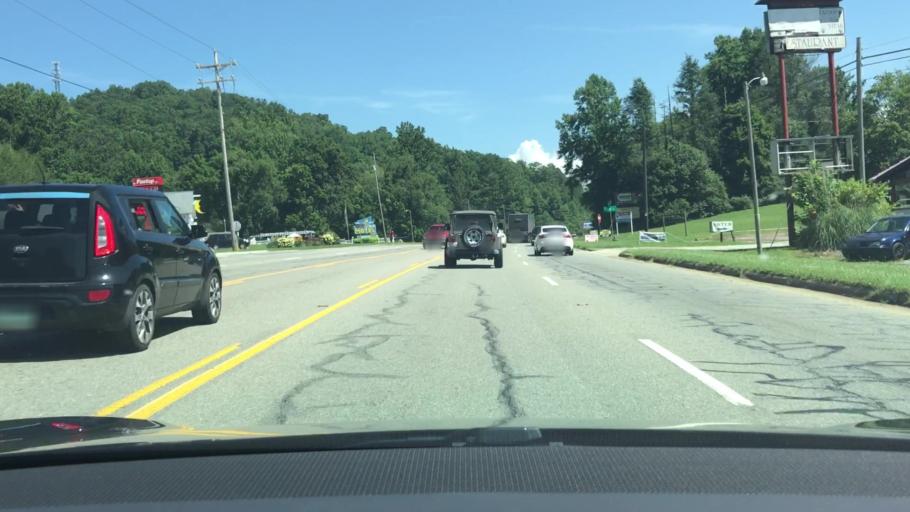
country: US
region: North Carolina
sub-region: Macon County
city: Franklin
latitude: 35.1383
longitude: -83.3983
